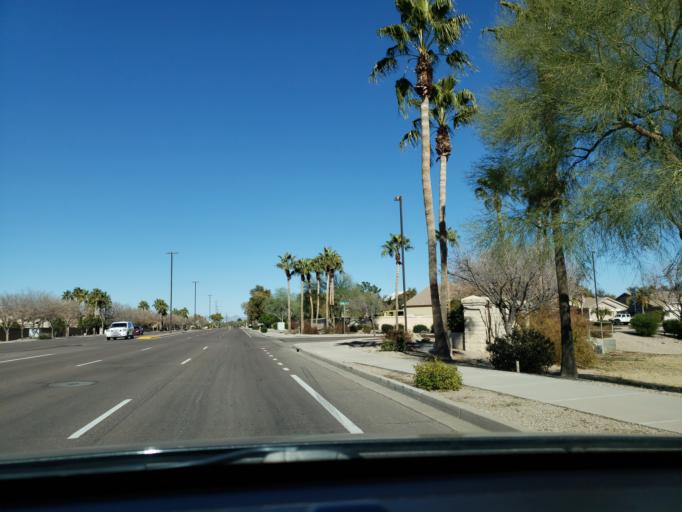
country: US
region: Arizona
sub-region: Maricopa County
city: Gilbert
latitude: 33.3234
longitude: -111.7897
